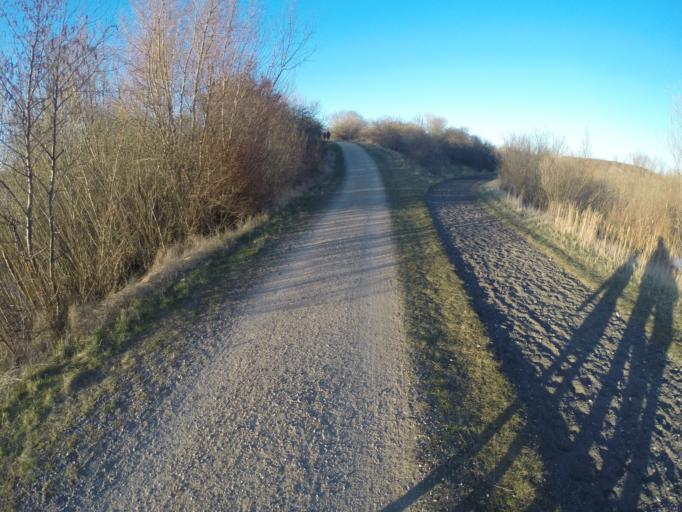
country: DK
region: Capital Region
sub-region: Hoje-Taastrup Kommune
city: Flong
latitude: 55.6352
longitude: 12.1872
